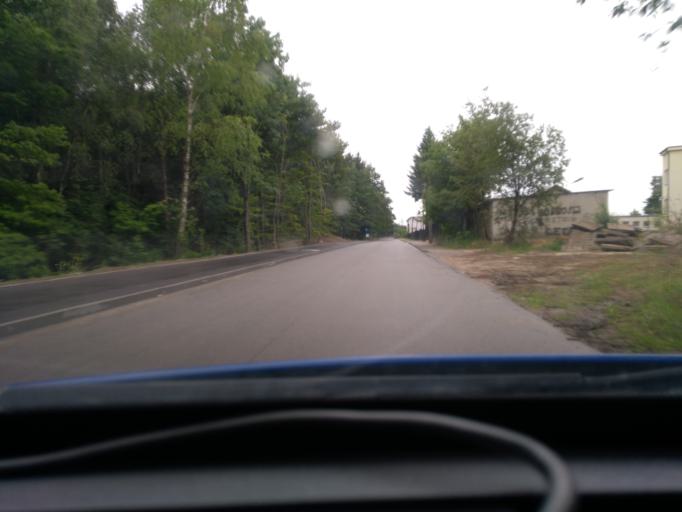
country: PL
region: Pomeranian Voivodeship
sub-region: Powiat kartuski
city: Kartuzy
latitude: 54.3424
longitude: 18.2073
